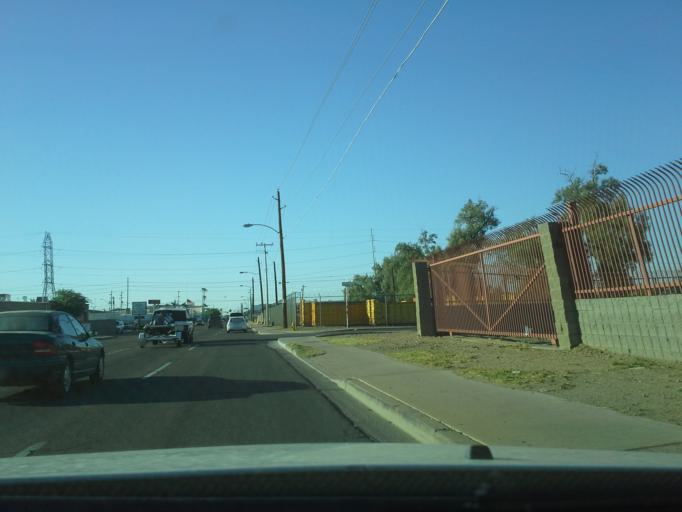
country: US
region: Arizona
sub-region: Maricopa County
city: Phoenix
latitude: 33.4381
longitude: -112.1000
